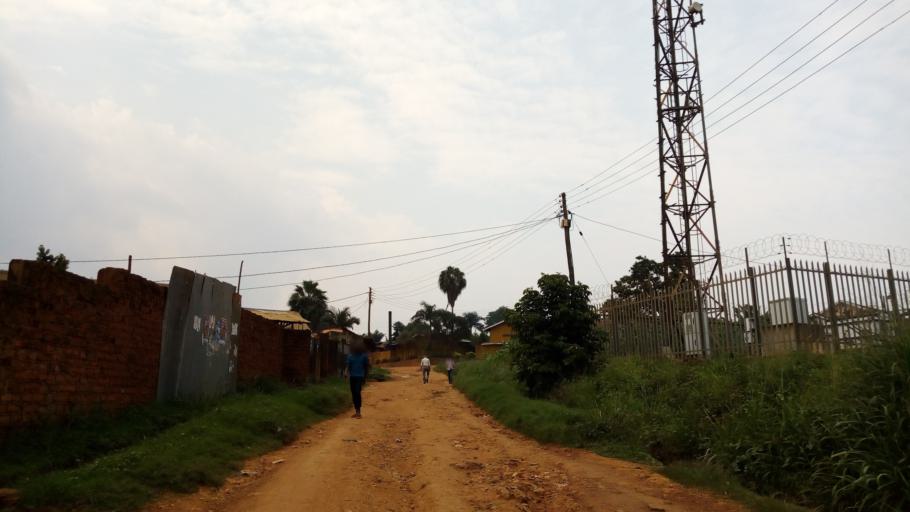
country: UG
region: Central Region
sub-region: Wakiso District
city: Kireka
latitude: 0.3175
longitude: 32.6365
